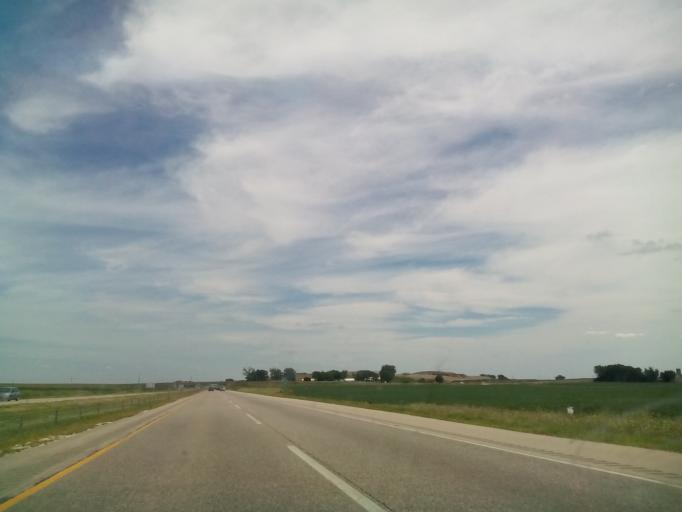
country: US
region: Illinois
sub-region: DeKalb County
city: Cortland
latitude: 41.9006
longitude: -88.6968
